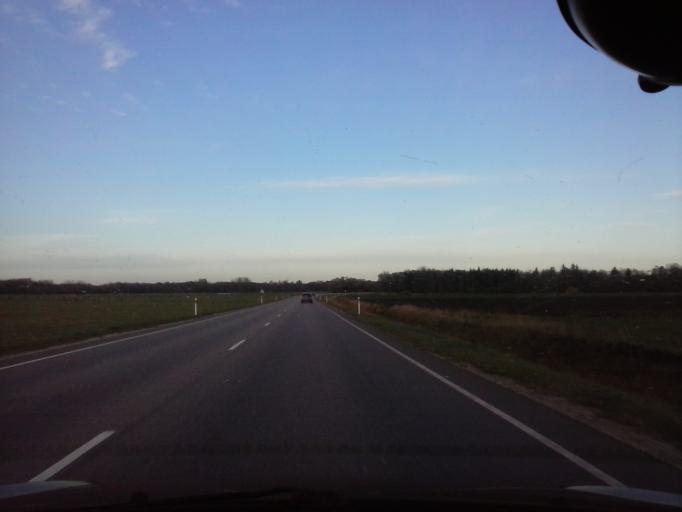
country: EE
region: Laeaene
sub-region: Ridala Parish
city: Uuemoisa
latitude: 58.9695
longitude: 23.8386
